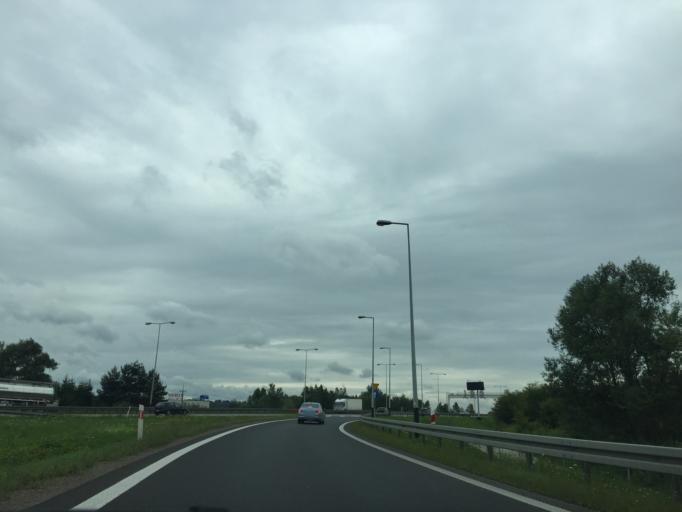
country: PL
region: Lesser Poland Voivodeship
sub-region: Powiat krakowski
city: Libertow
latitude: 49.9923
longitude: 19.9108
